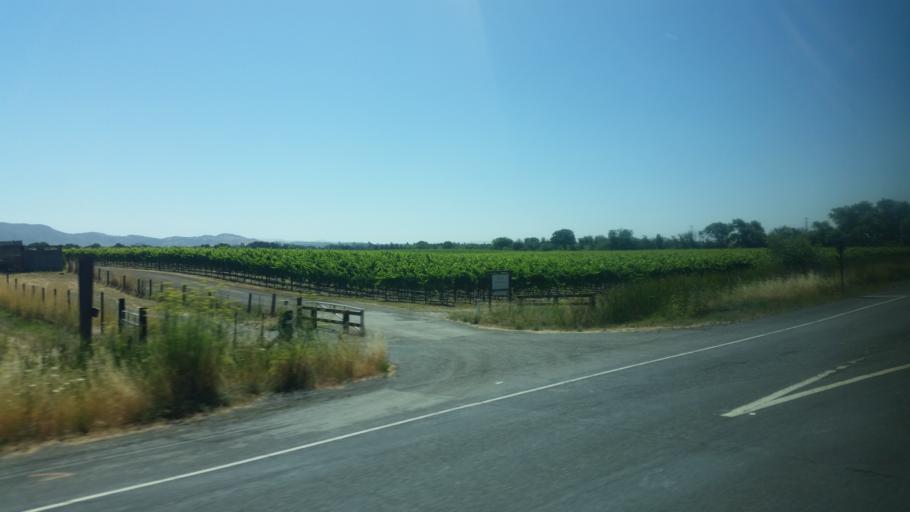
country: US
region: California
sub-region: Sonoma County
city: Temelec
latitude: 38.2565
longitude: -122.4803
